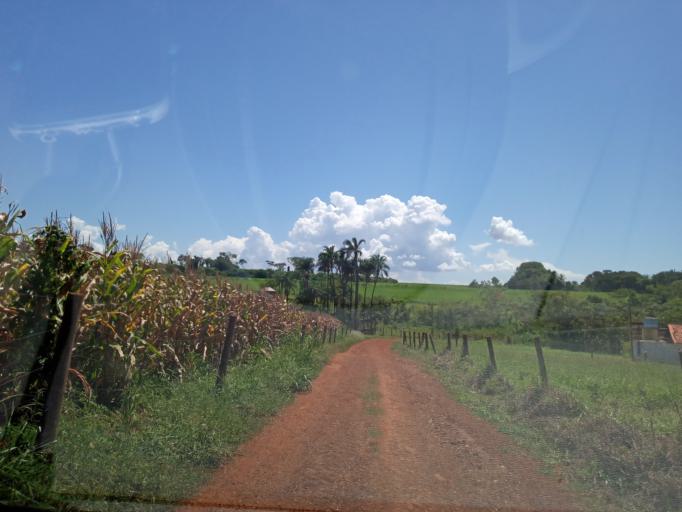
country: BR
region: Goias
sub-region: Itumbiara
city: Itumbiara
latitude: -18.4372
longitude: -49.1685
